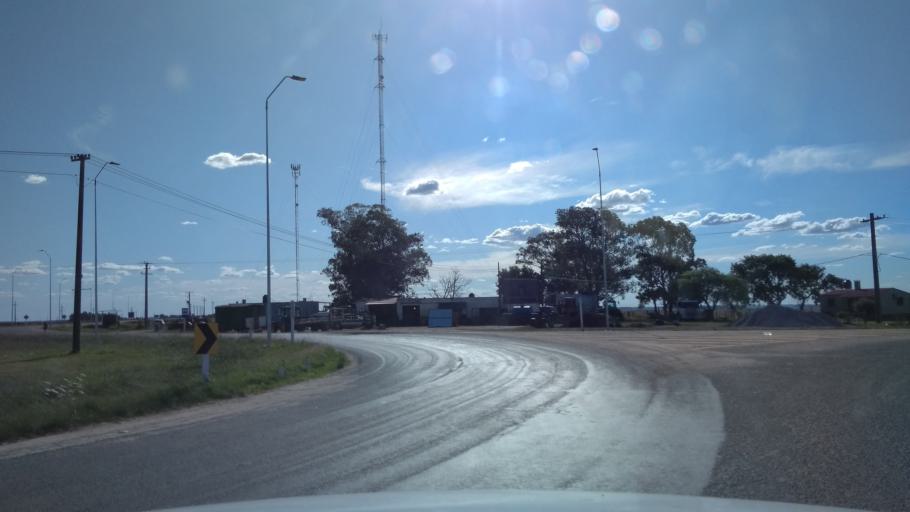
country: UY
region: Florida
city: Casupa
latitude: -34.0362
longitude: -55.8866
